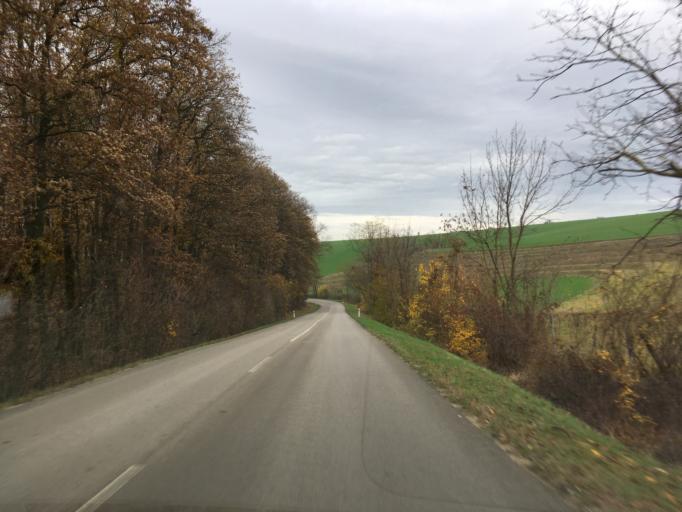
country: SK
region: Nitriansky
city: Svodin
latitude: 48.0331
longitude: 18.3880
